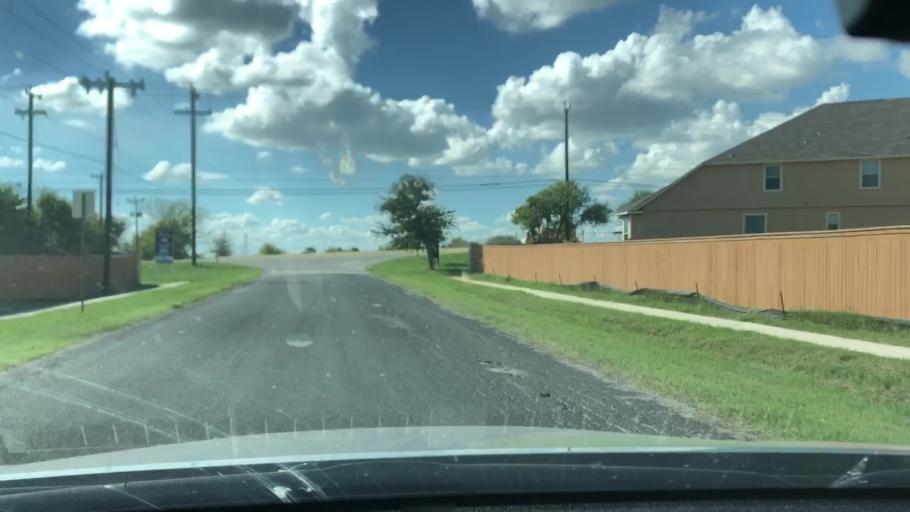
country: US
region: Texas
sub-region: Bexar County
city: Converse
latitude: 29.4705
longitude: -98.3125
